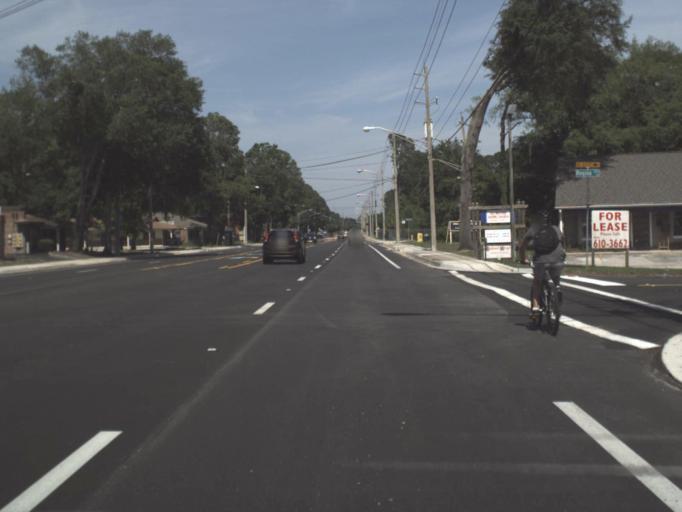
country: US
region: Florida
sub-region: Clay County
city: Orange Park
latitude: 30.2187
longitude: -81.6104
